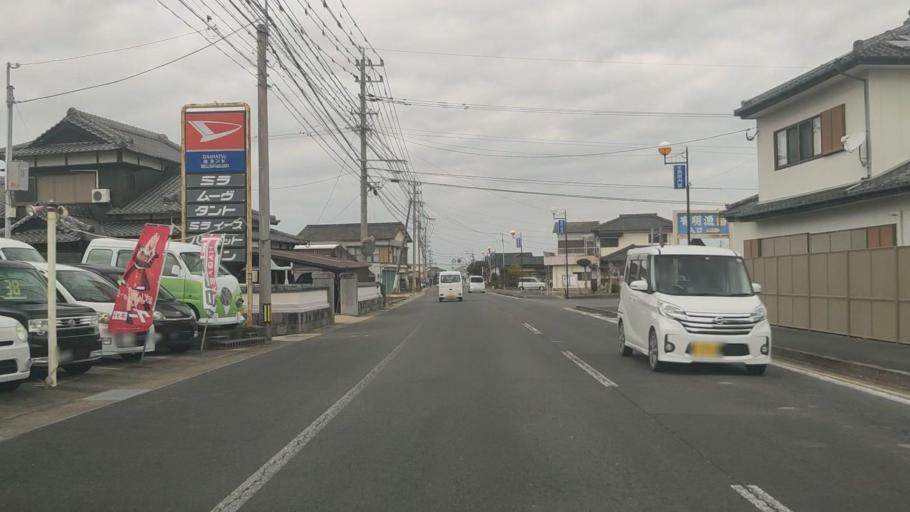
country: JP
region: Nagasaki
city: Shimabara
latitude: 32.8640
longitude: 130.3228
